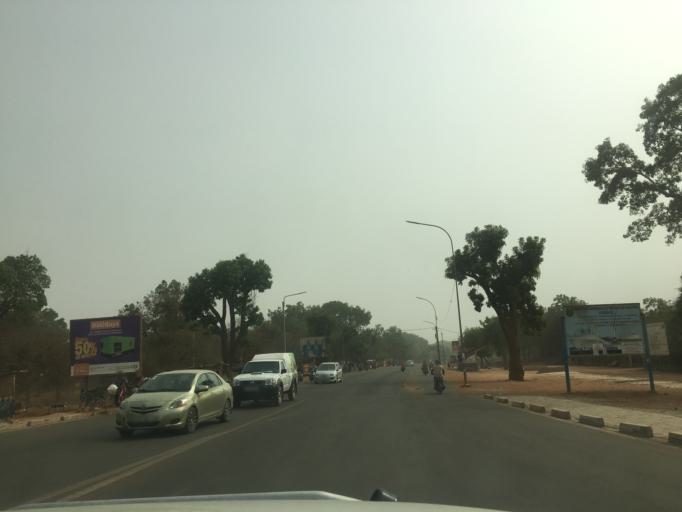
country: BF
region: Centre
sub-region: Kadiogo Province
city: Ouagadougou
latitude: 12.3967
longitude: -1.4978
